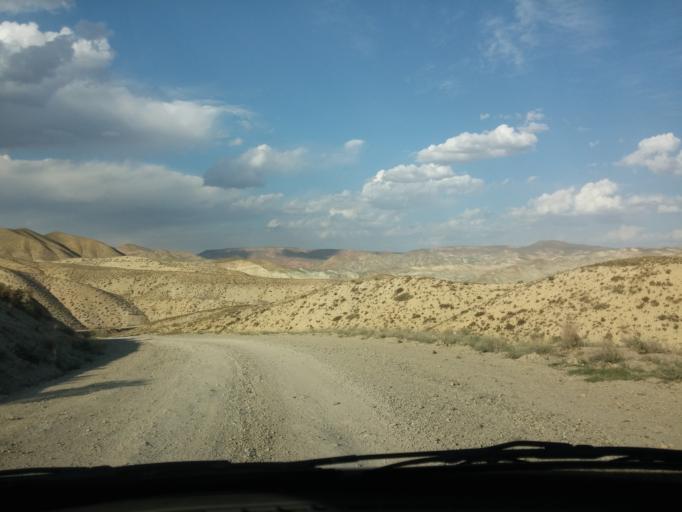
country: IR
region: Tehran
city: Damavand
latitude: 35.5369
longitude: 52.2110
